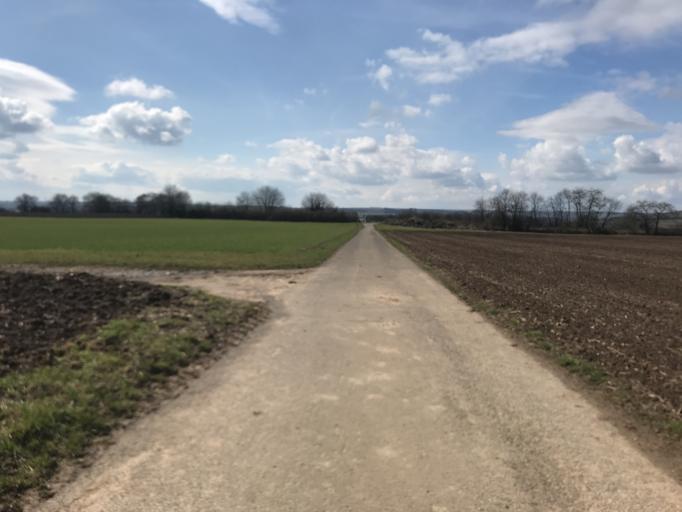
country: DE
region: Rheinland-Pfalz
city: Klein-Winternheim
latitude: 49.9288
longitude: 8.2033
